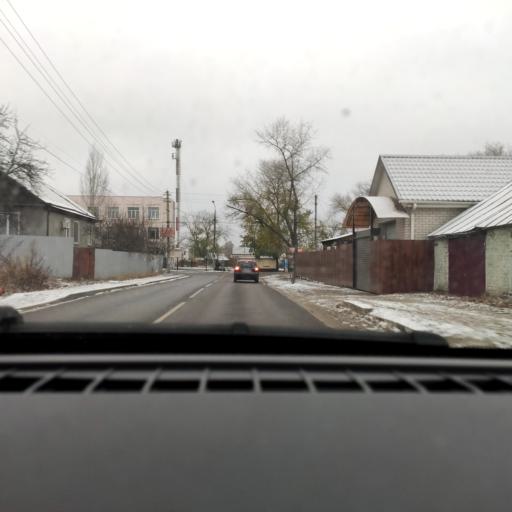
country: RU
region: Voronezj
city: Somovo
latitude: 51.7357
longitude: 39.2691
